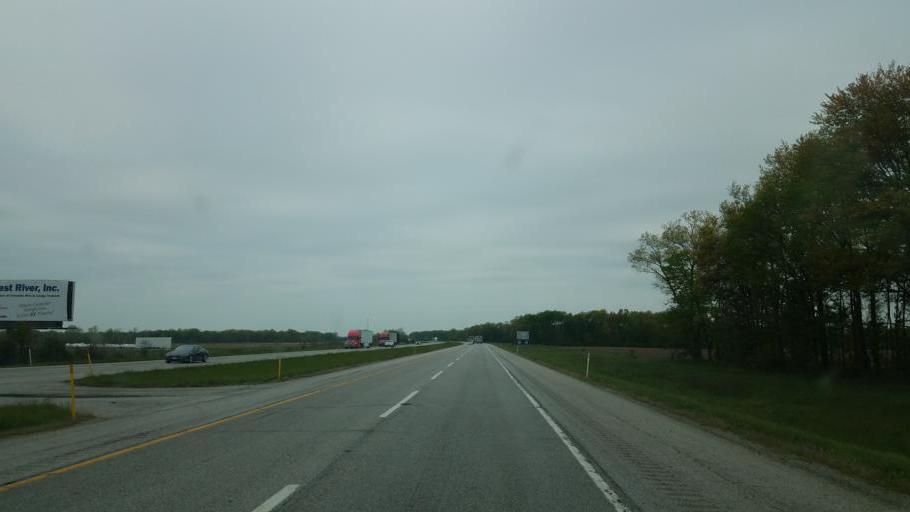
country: US
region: Indiana
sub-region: Elkhart County
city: Middlebury
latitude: 41.7472
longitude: -85.6973
